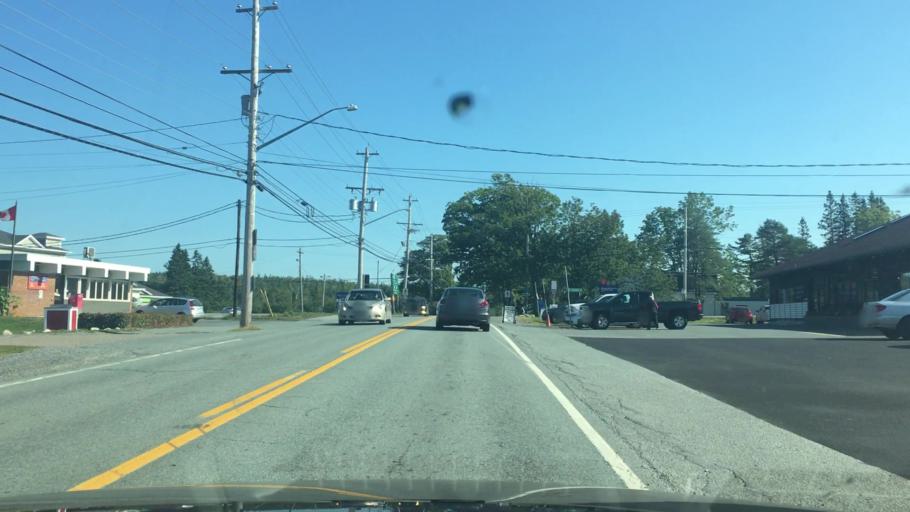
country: CA
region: Nova Scotia
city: Cole Harbour
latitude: 44.7862
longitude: -63.1492
